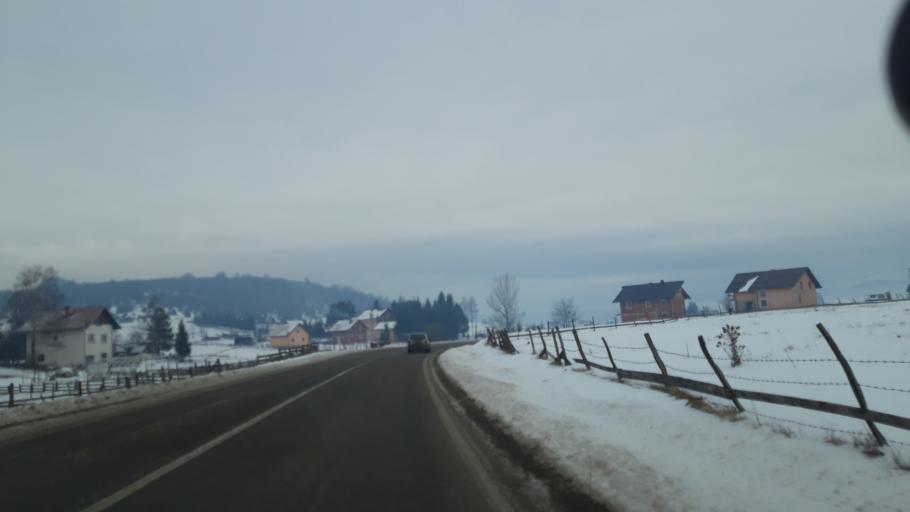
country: BA
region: Republika Srpska
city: Sokolac
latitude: 43.9423
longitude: 18.8320
